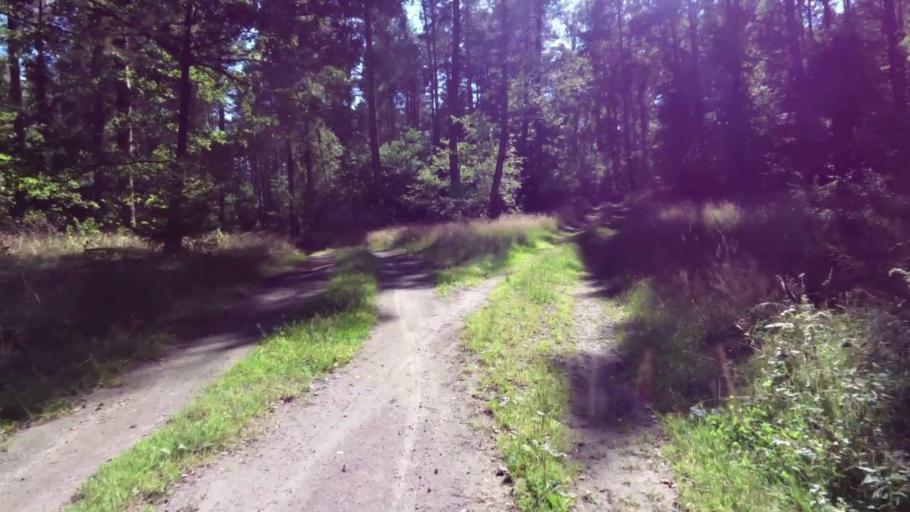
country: PL
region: West Pomeranian Voivodeship
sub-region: Powiat szczecinecki
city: Borne Sulinowo
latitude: 53.6030
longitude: 16.6073
